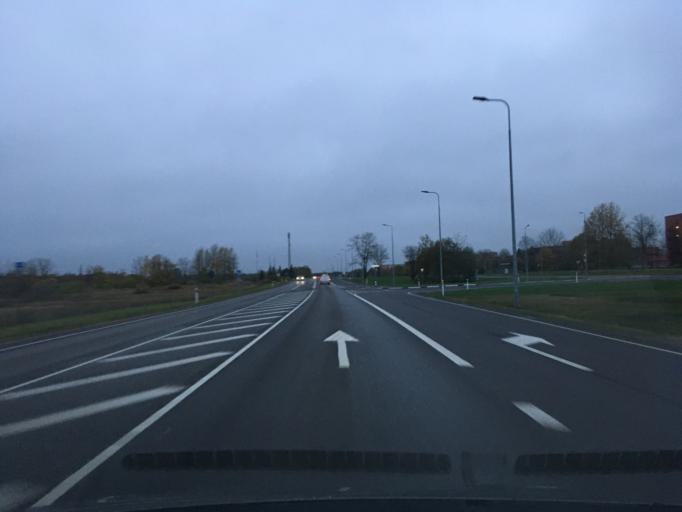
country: EE
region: Ida-Virumaa
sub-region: Sillamaee linn
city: Sillamae
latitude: 59.3892
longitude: 27.7978
